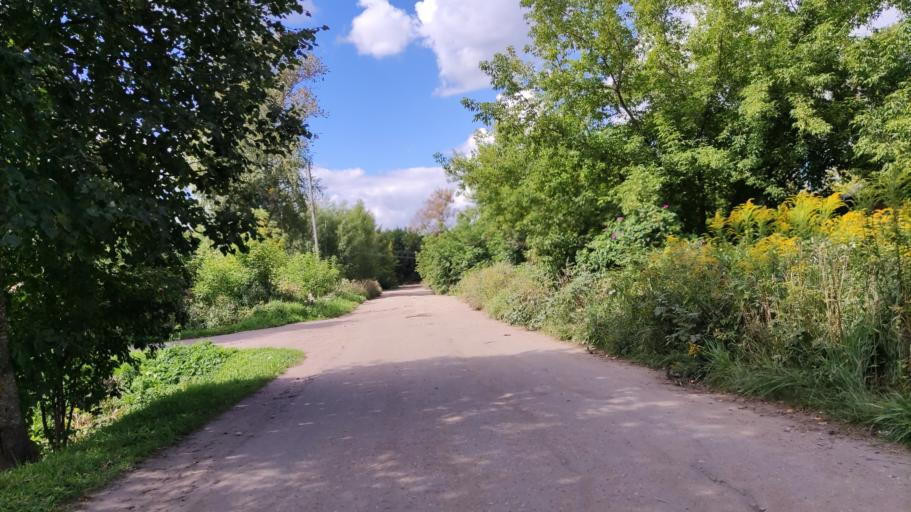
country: RU
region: Tverskaya
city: Rzhev
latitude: 56.2383
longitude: 34.3165
